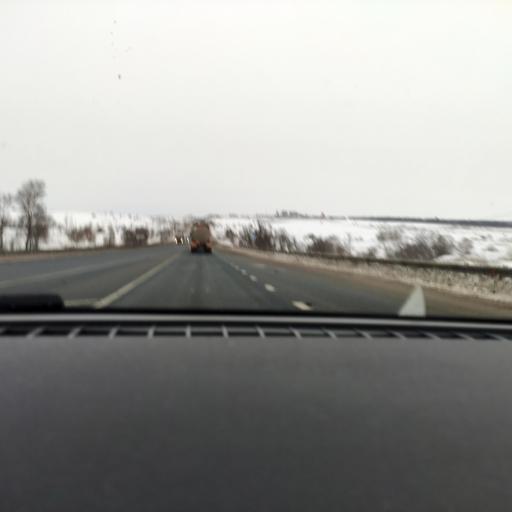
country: RU
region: Samara
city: Novosemeykino
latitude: 53.3770
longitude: 50.4323
